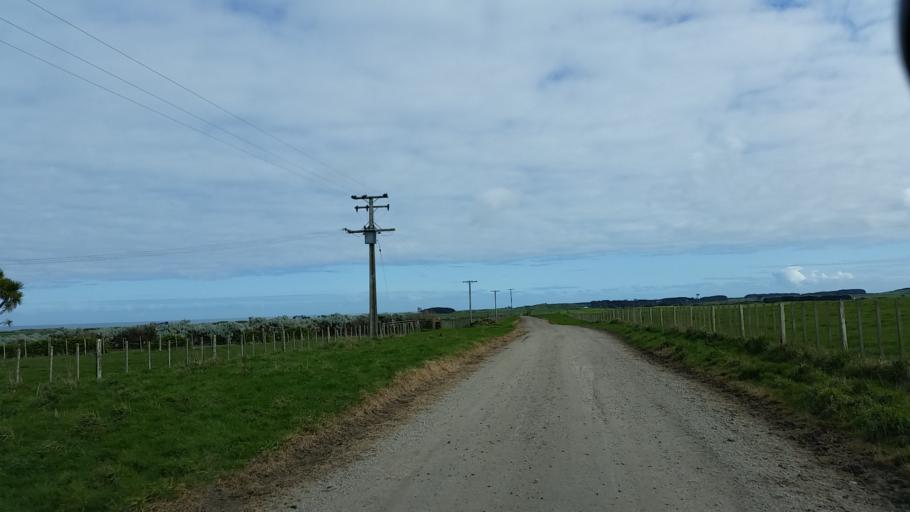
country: NZ
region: Taranaki
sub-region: South Taranaki District
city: Patea
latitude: -39.8070
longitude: 174.6516
